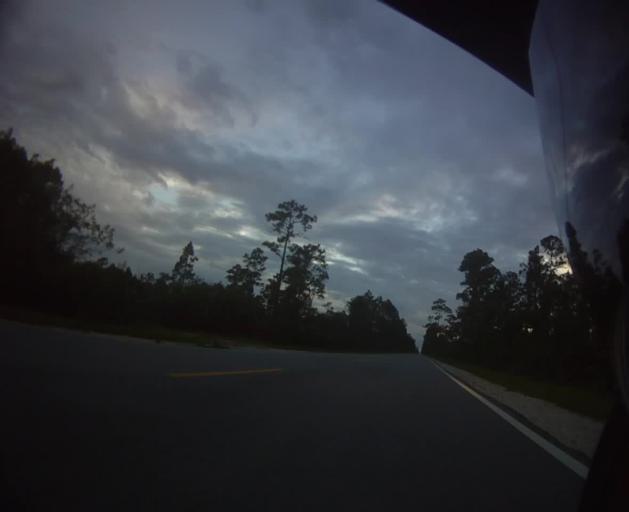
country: US
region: Florida
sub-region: Miami-Dade County
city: Florida City
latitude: 25.3894
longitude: -80.6500
